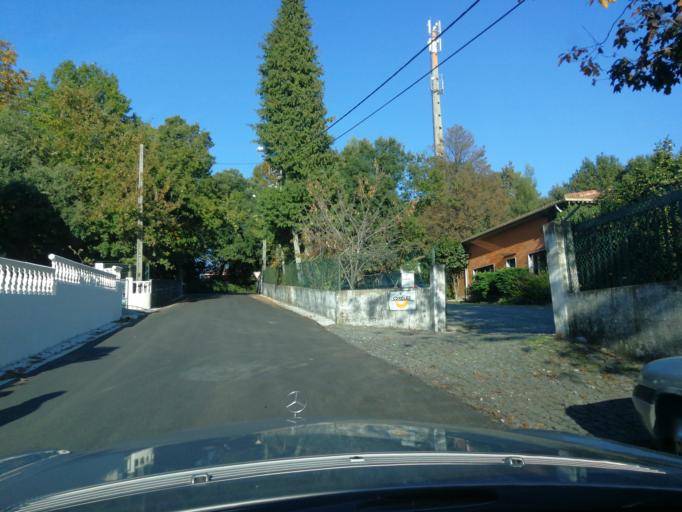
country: PT
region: Braga
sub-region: Vila Nova de Famalicao
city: Vila Nova de Famalicao
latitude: 41.4296
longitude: -8.5159
